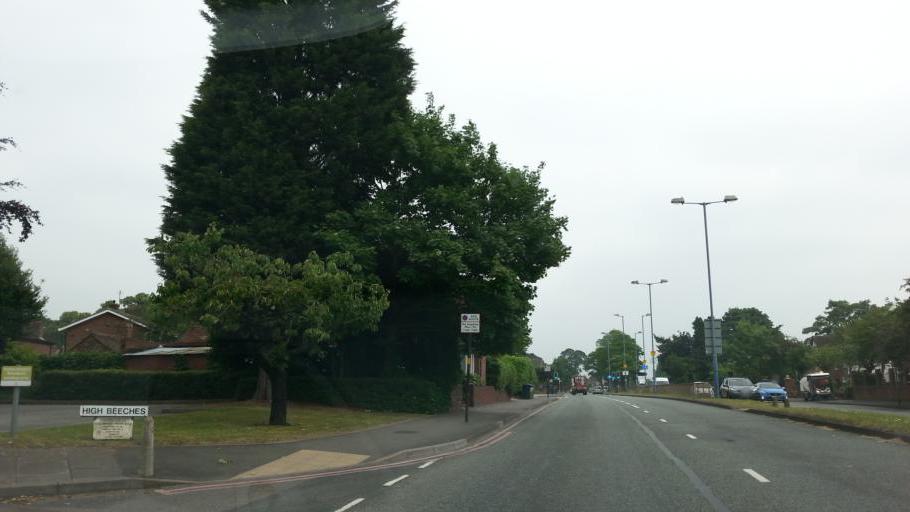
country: GB
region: England
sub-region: City and Borough of Birmingham
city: Hockley
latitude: 52.5446
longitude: -1.9440
